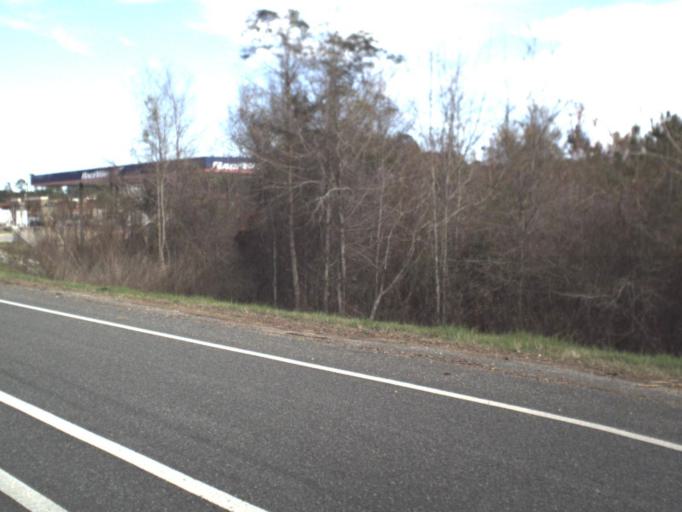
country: US
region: Florida
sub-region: Washington County
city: Chipley
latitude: 30.7472
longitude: -85.3842
